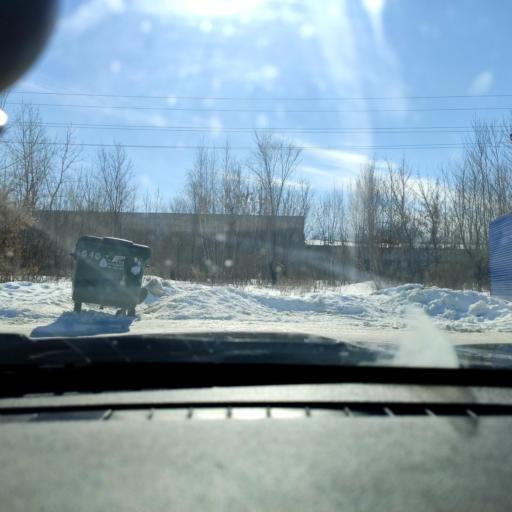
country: RU
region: Samara
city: Tol'yatti
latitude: 53.5656
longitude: 49.3219
